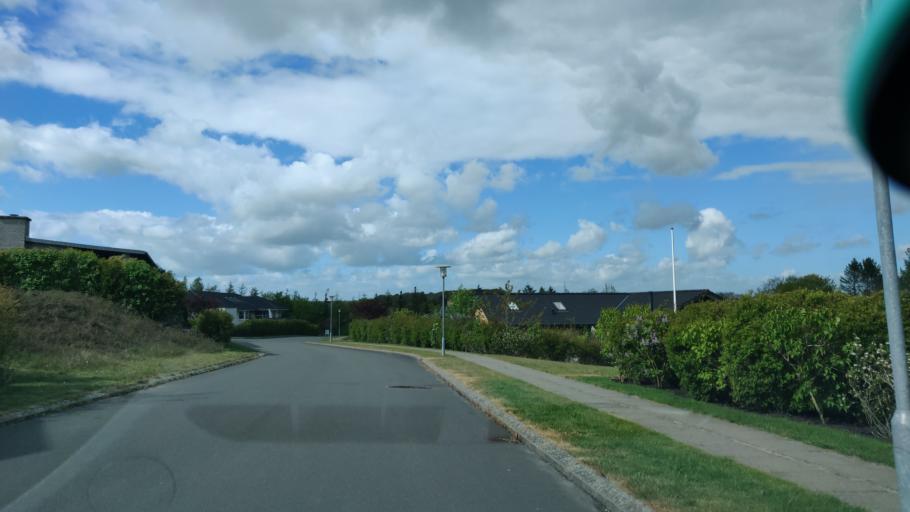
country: DK
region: South Denmark
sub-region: Kolding Kommune
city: Kolding
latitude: 55.5644
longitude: 9.4155
